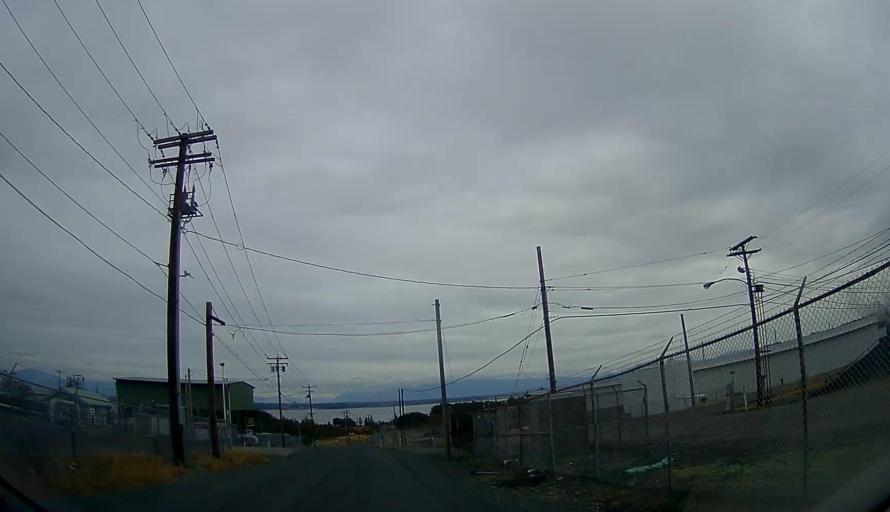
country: US
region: Washington
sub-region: Skagit County
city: Anacortes
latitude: 48.4783
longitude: -122.5602
